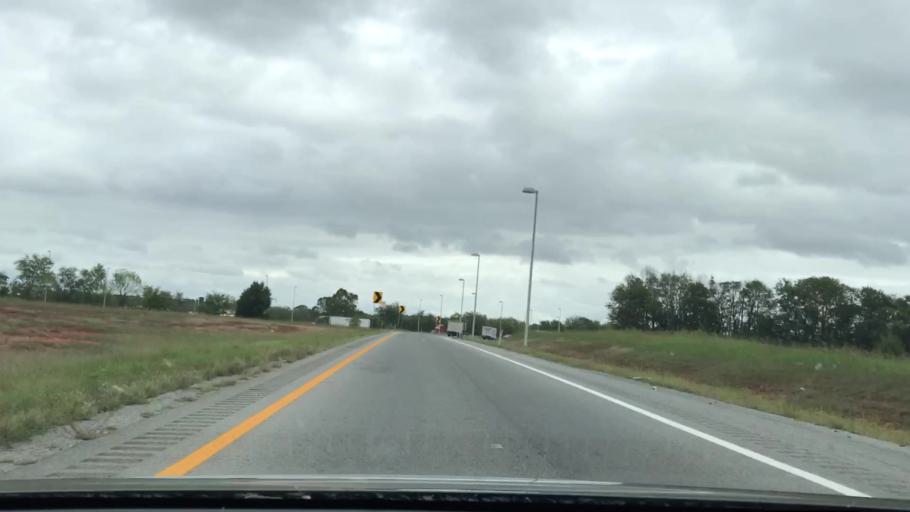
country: US
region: Kentucky
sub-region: Christian County
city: Fort Campbell North
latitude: 36.7382
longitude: -87.5047
